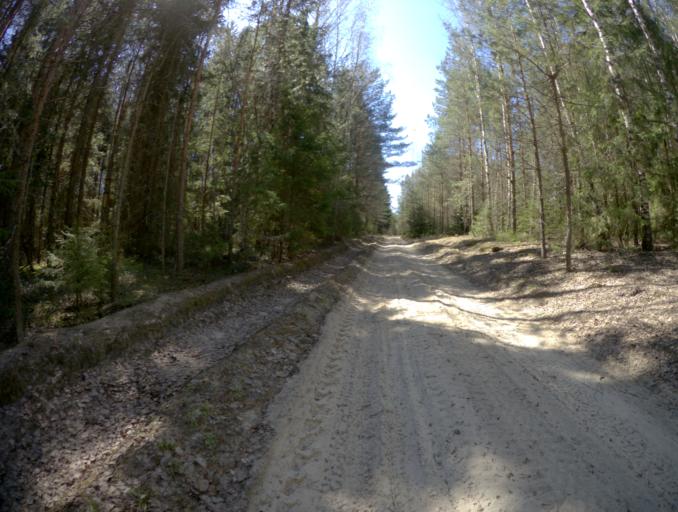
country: RU
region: Vladimir
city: Golovino
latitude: 55.8944
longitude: 40.4169
